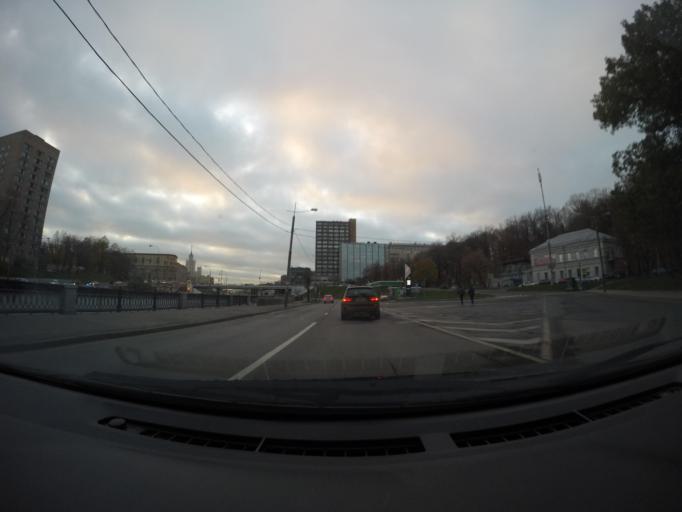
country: RU
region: Moscow
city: Taganskiy
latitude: 55.7505
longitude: 37.6598
